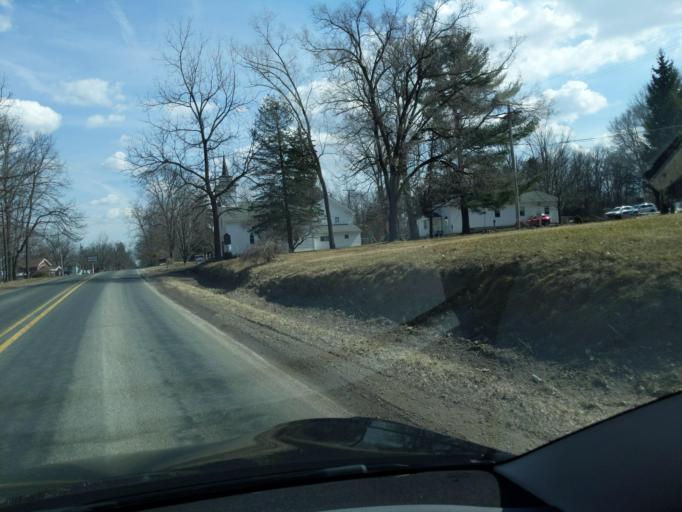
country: US
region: Michigan
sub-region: Washtenaw County
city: Chelsea
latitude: 42.3854
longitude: -84.0098
